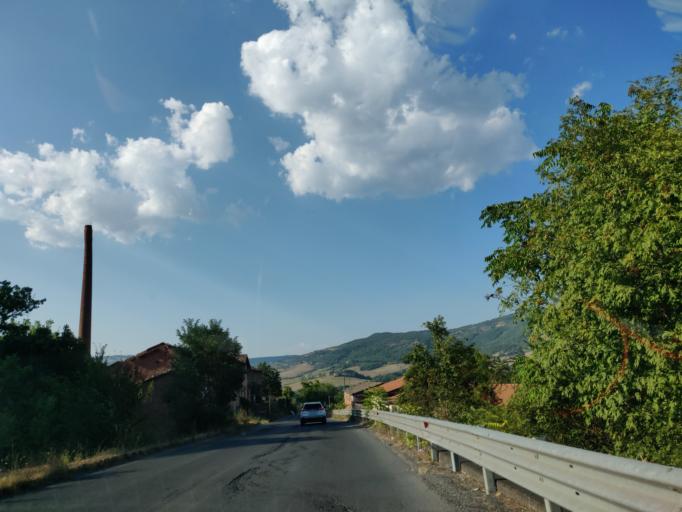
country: IT
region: Latium
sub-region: Provincia di Viterbo
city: Acquapendente
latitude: 42.7538
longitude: 11.8655
